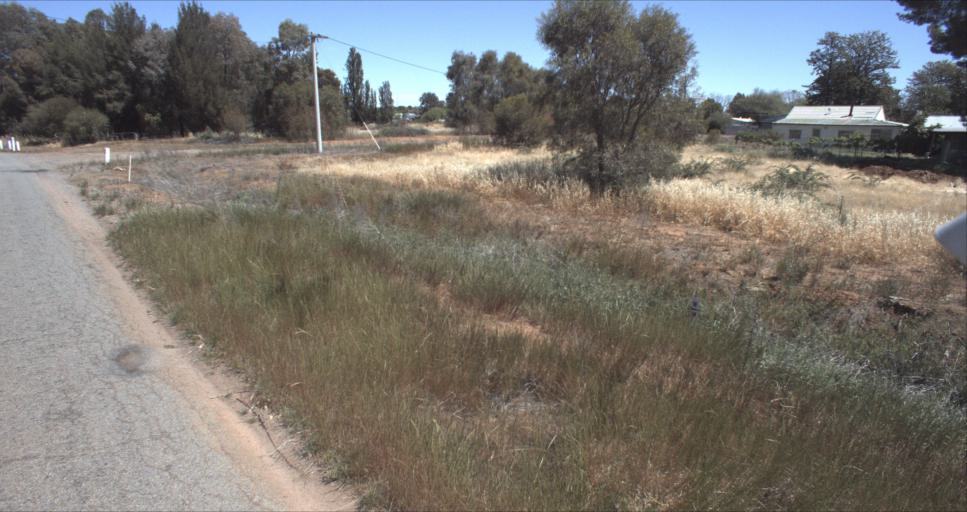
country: AU
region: New South Wales
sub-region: Leeton
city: Leeton
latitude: -34.5277
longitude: 146.3332
